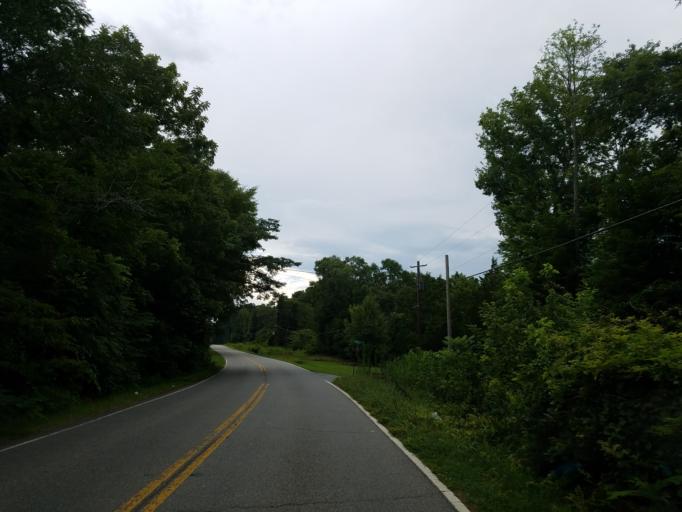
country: US
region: Georgia
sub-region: Bartow County
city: Cartersville
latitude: 34.2534
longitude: -84.8531
